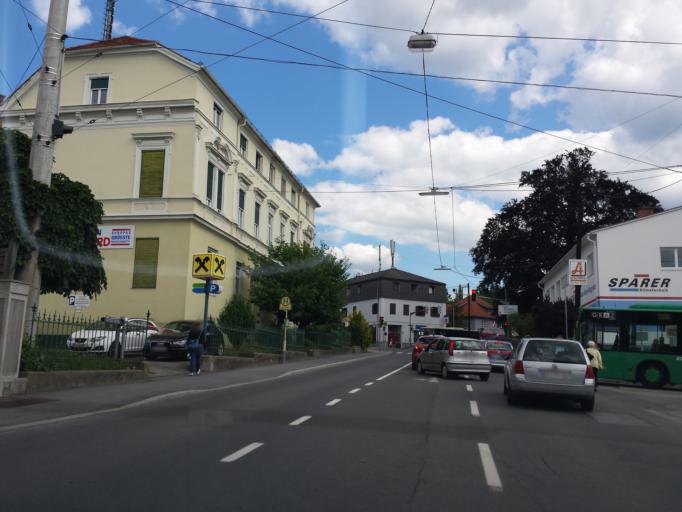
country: AT
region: Styria
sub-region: Graz Stadt
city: Graz
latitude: 47.0893
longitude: 15.4599
